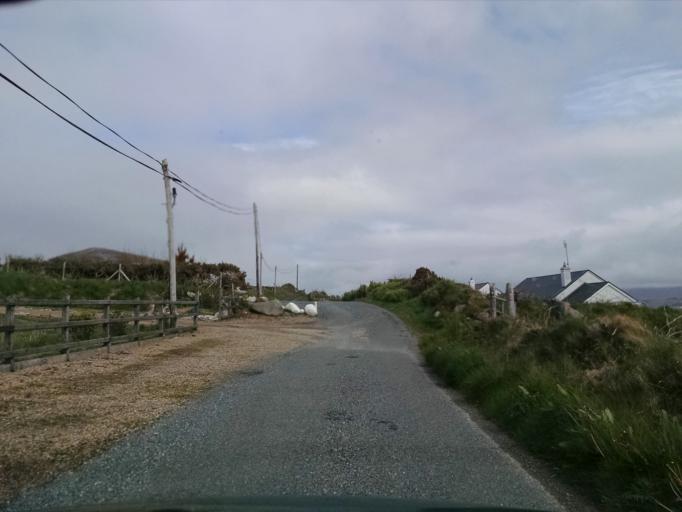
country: IE
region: Connaught
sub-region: County Galway
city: Clifden
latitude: 53.7627
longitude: -9.8691
